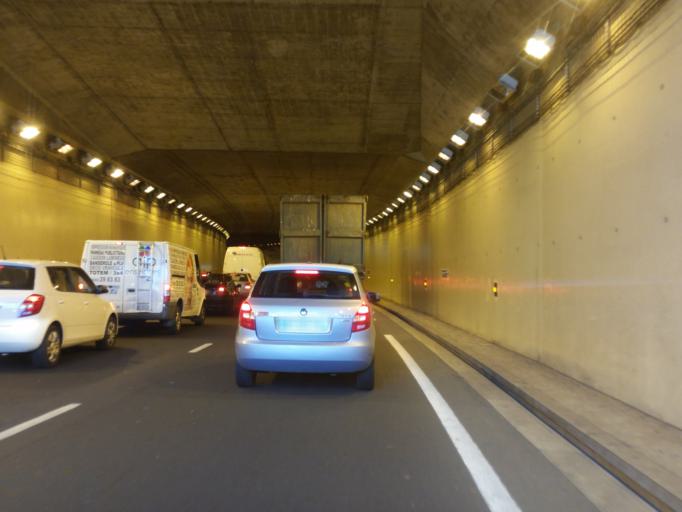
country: RE
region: Reunion
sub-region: Reunion
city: Saint-Denis
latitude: -20.8910
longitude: 55.4571
